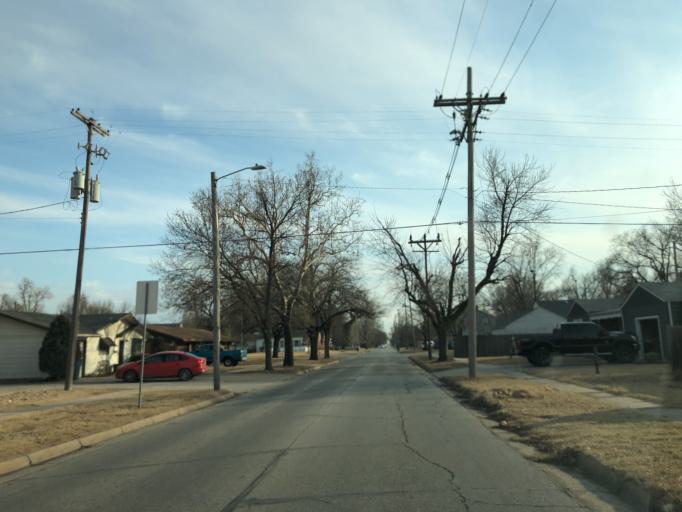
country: US
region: Kansas
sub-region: Reno County
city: Hutchinson
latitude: 38.0798
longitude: -97.9356
